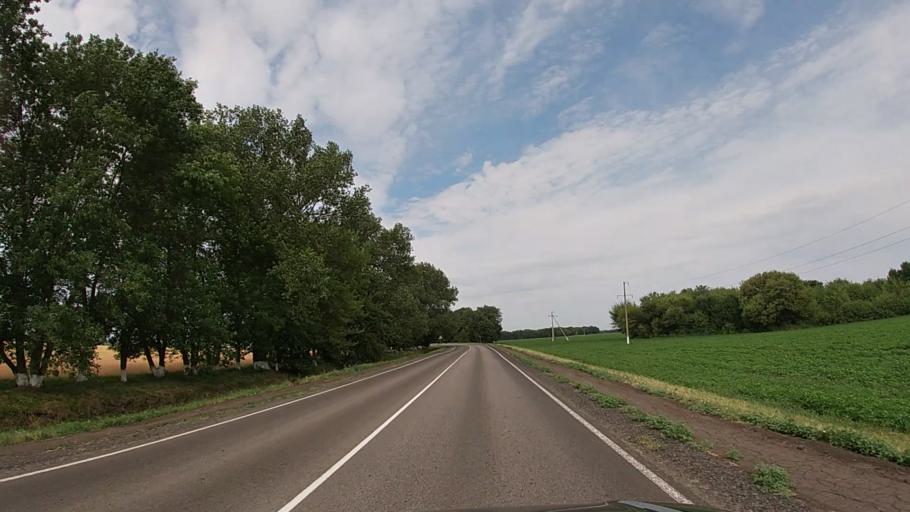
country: RU
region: Belgorod
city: Krasnaya Yaruga
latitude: 50.8106
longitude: 35.5129
